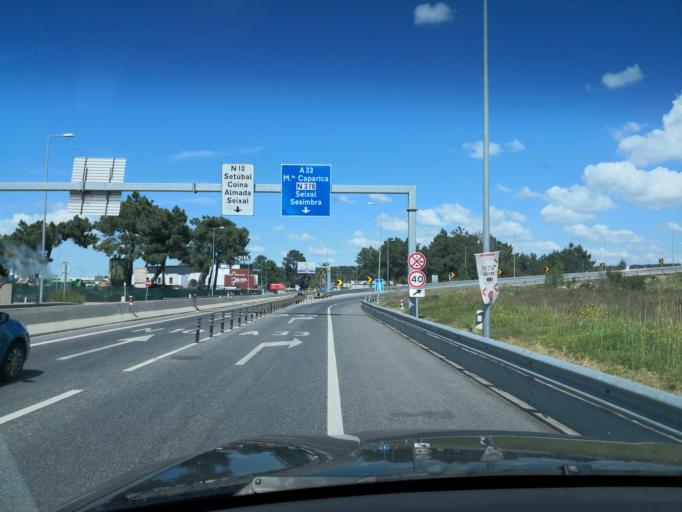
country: PT
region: Setubal
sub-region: Seixal
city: Aldeia de Paio Pires
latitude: 38.5948
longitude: -9.0533
